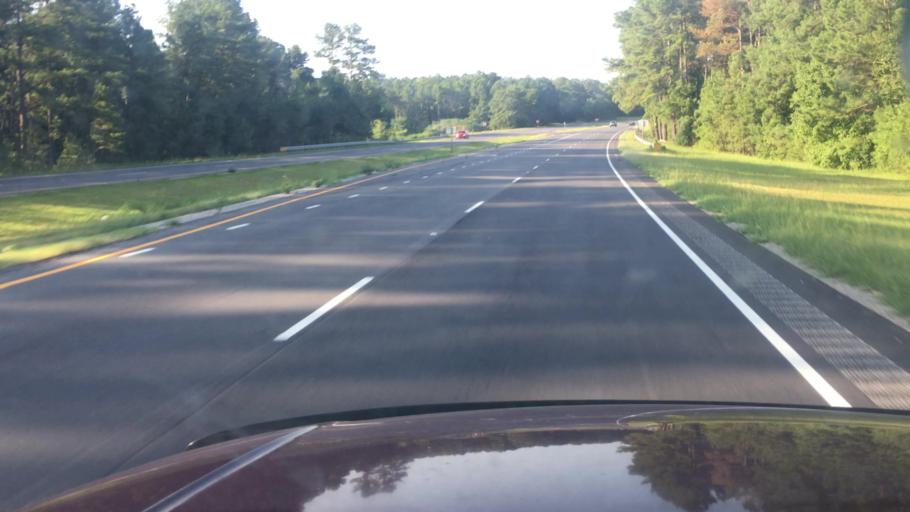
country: US
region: North Carolina
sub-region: Robeson County
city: Saint Pauls
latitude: 34.8600
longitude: -78.8497
